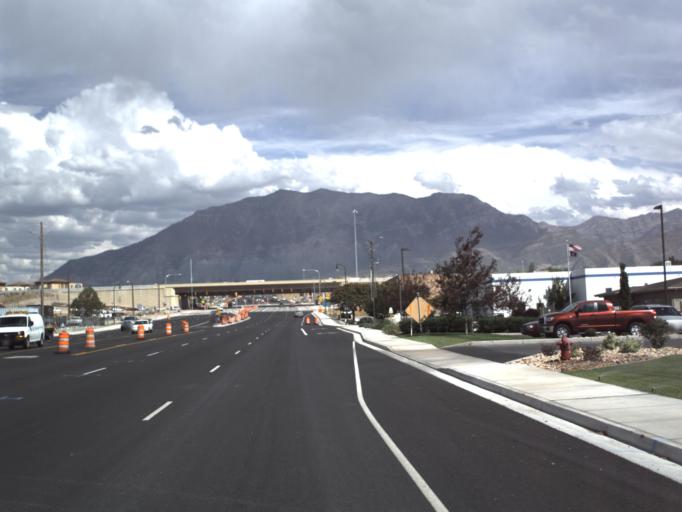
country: US
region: Utah
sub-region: Utah County
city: Lindon
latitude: 40.3118
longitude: -111.7335
